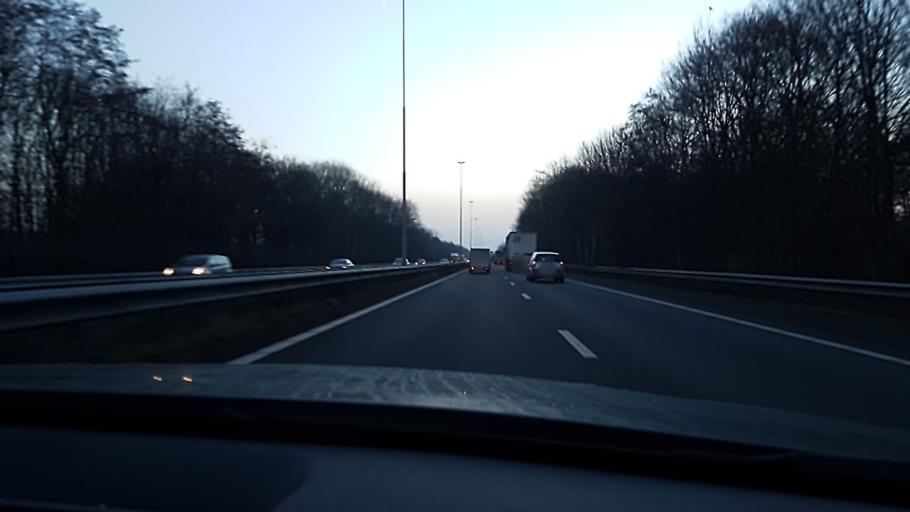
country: NL
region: North Brabant
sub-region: Gemeente Oosterhout
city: Oosterhout
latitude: 51.6220
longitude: 4.8658
